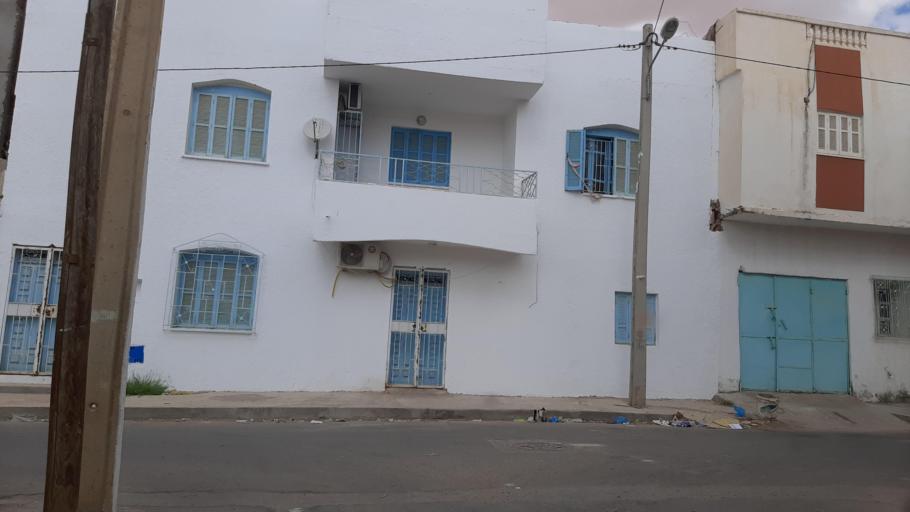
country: TN
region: Tataouine
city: Tataouine
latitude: 32.9334
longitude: 10.4492
